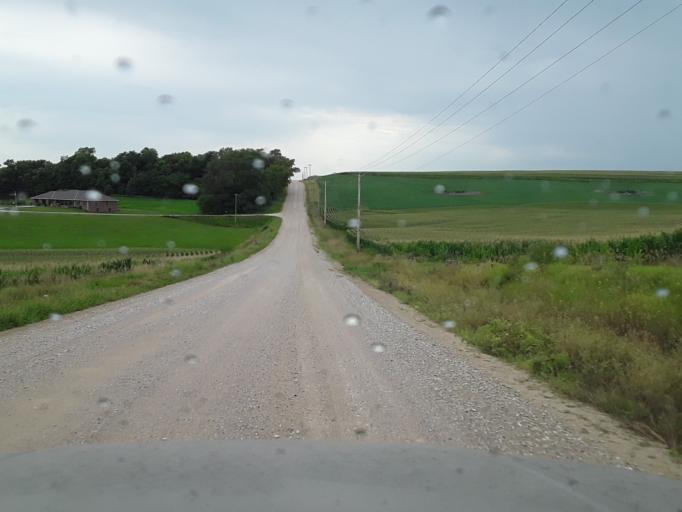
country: US
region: Nebraska
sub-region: Washington County
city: Blair
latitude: 41.5091
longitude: -96.1804
